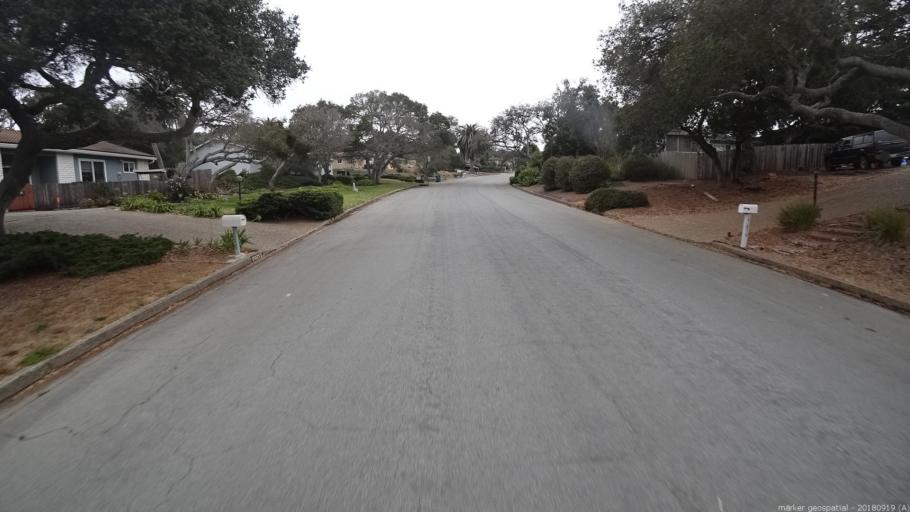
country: US
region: California
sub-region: Monterey County
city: Prunedale
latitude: 36.7812
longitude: -121.7018
